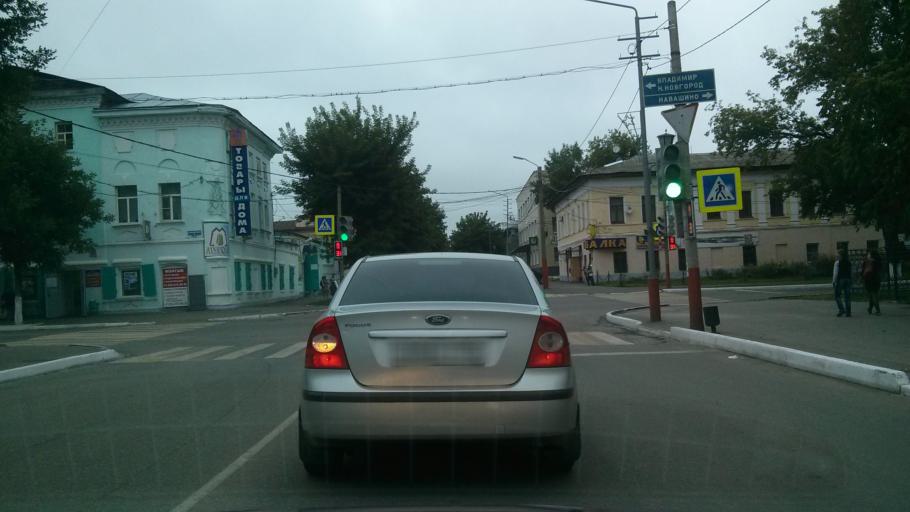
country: RU
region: Vladimir
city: Murom
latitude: 55.5802
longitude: 42.0517
